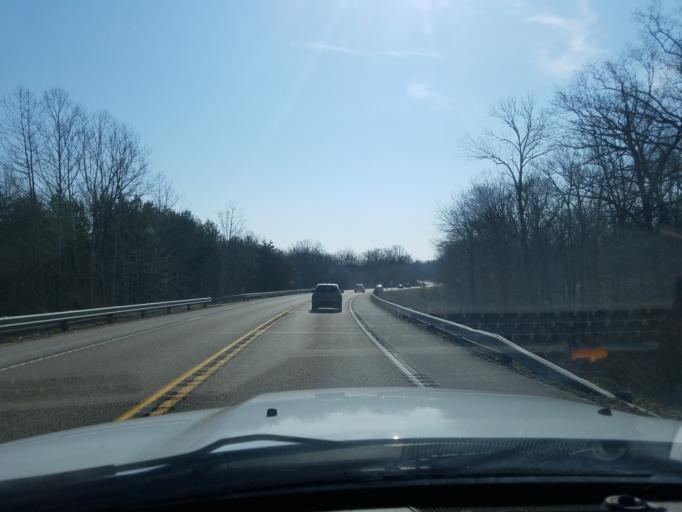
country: US
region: Indiana
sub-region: Bartholomew County
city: Lowell
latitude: 39.2004
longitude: -86.0223
